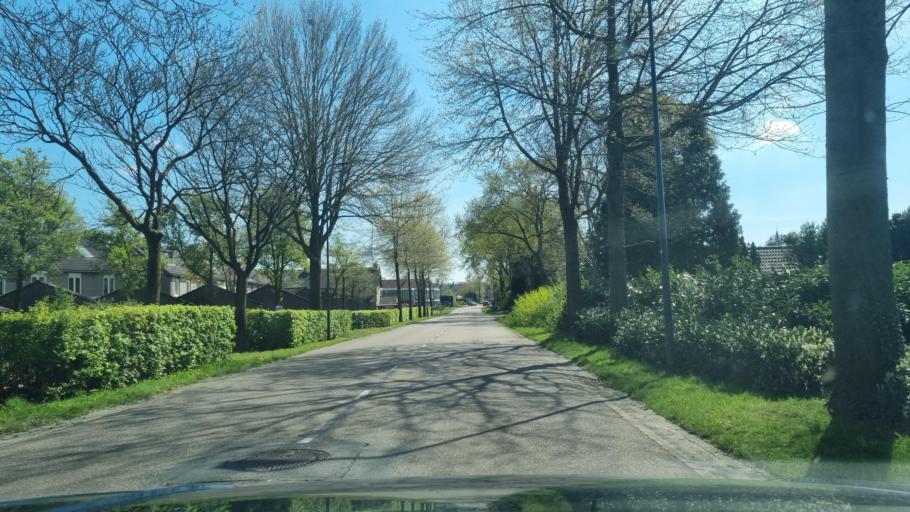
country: NL
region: North Brabant
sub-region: Gemeente 's-Hertogenbosch
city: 's-Hertogenbosch
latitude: 51.7219
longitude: 5.3634
